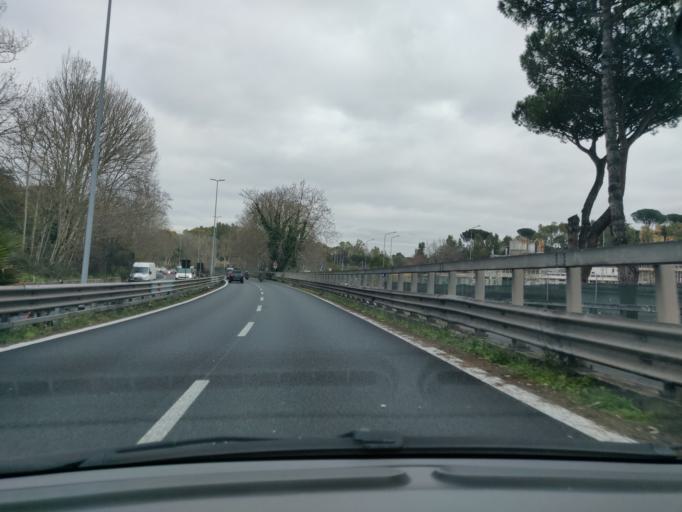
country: IT
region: Latium
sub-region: Citta metropolitana di Roma Capitale
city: La Massimina-Casal Lumbroso
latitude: 41.8840
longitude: 12.3935
